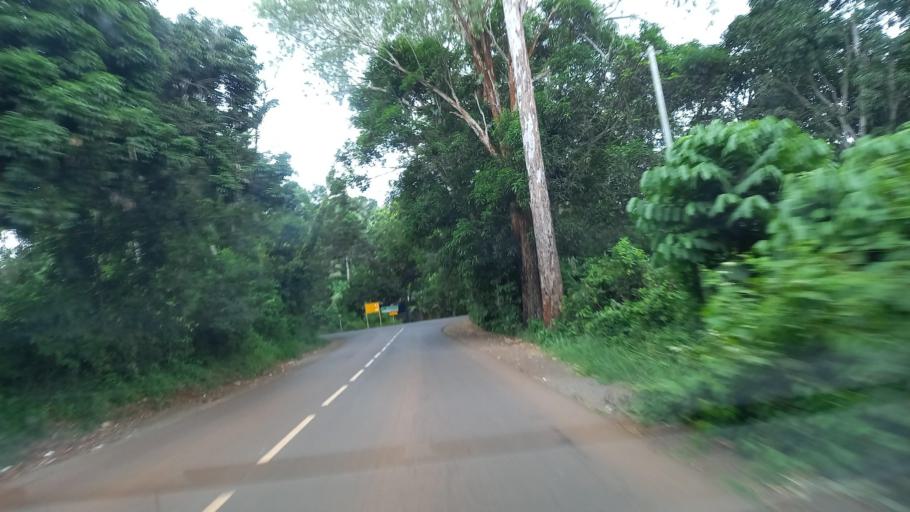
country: YT
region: Ouangani
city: Ouangani
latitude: -12.8335
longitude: 45.1390
